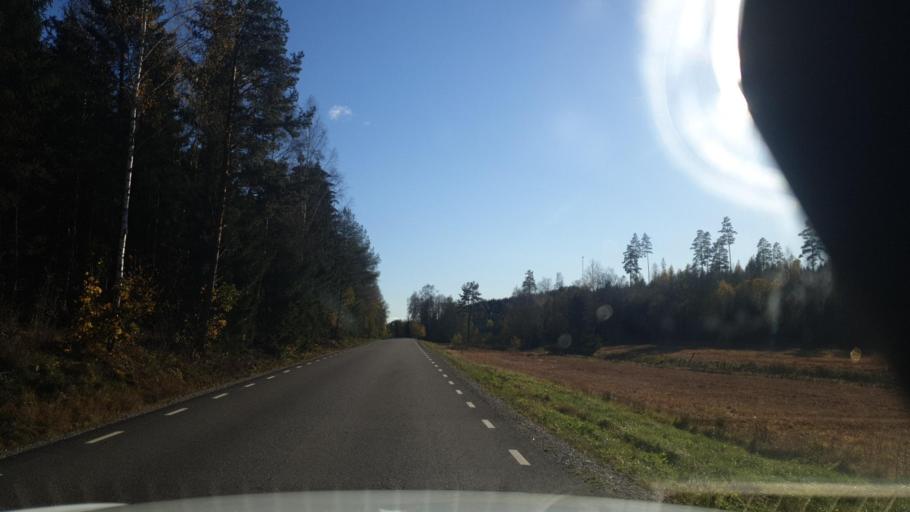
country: SE
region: Vaermland
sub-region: Arvika Kommun
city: Arvika
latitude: 59.6646
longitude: 12.7974
